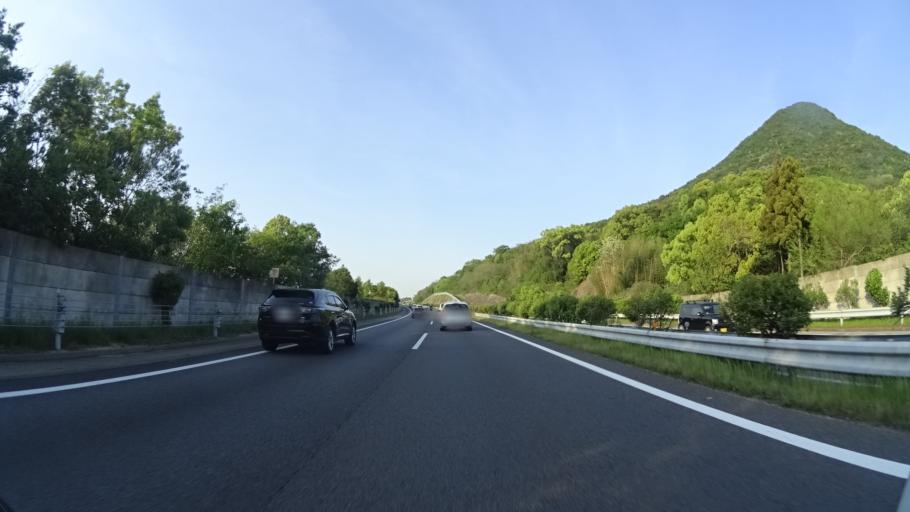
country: JP
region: Kagawa
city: Sakaidecho
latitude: 34.2750
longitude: 133.8359
